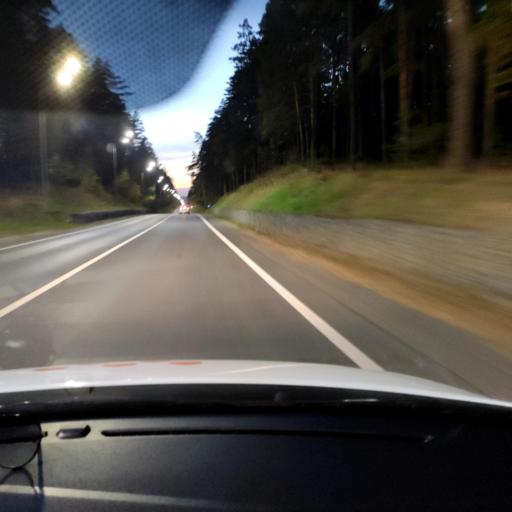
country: RU
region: Tatarstan
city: Verkhniy Uslon
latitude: 55.6369
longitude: 49.0579
